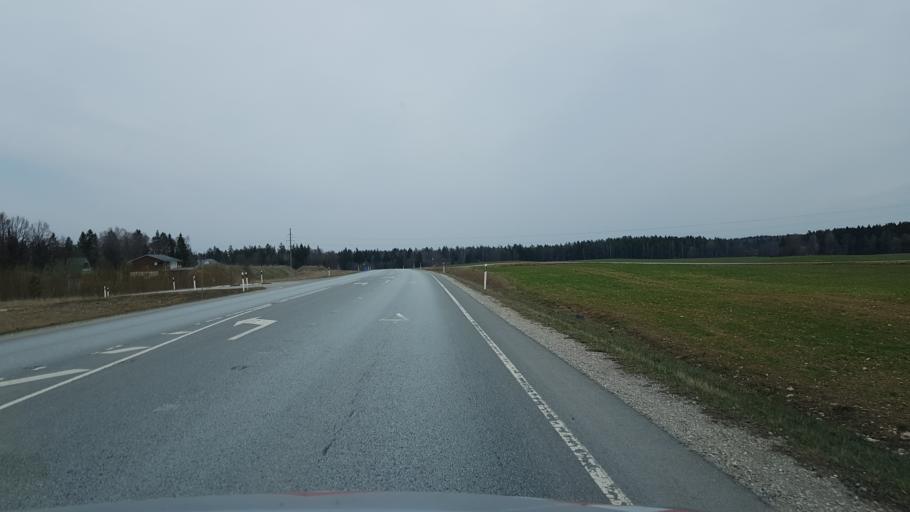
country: EE
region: Laeaene-Virumaa
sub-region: Rakvere linn
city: Rakvere
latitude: 59.3264
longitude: 26.3935
